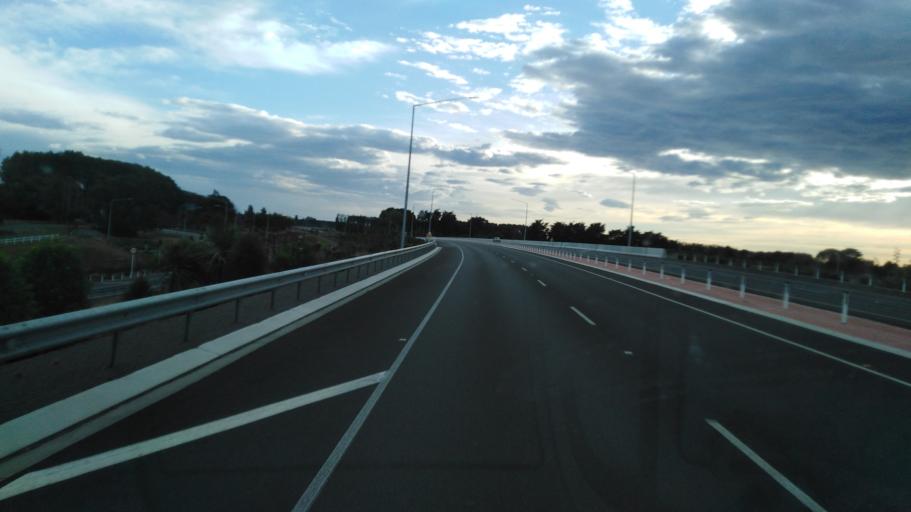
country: NZ
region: Canterbury
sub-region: Waimakariri District
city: Kaiapoi
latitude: -43.4512
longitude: 172.6089
